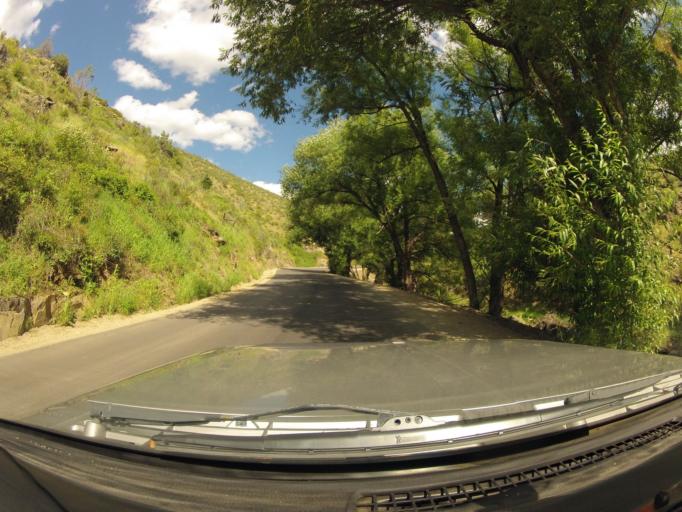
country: US
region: Colorado
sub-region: Larimer County
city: Laporte
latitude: 40.5577
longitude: -105.2933
